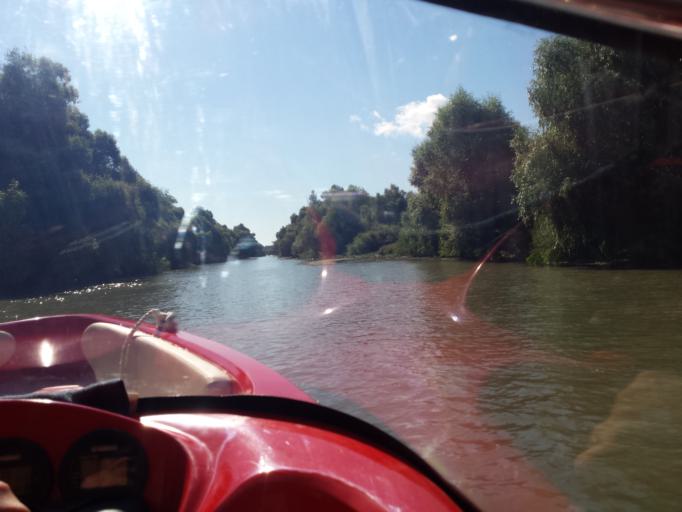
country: RO
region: Tulcea
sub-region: Comuna Pardina
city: Pardina
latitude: 45.2525
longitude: 28.9796
